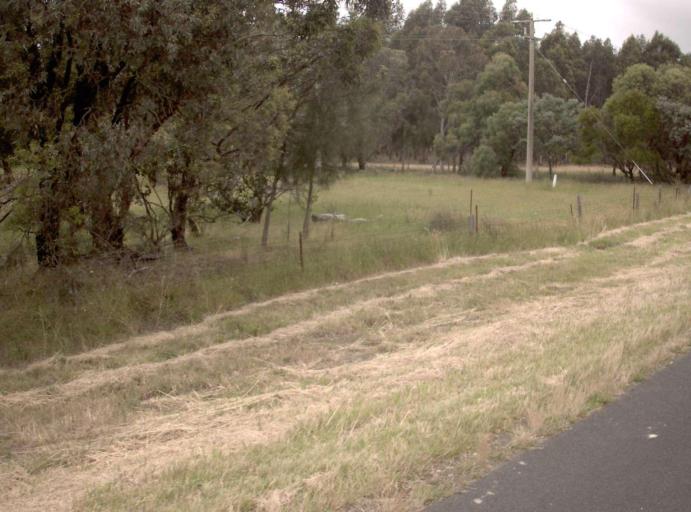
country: AU
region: Victoria
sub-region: Latrobe
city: Morwell
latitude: -38.2738
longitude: 146.4216
